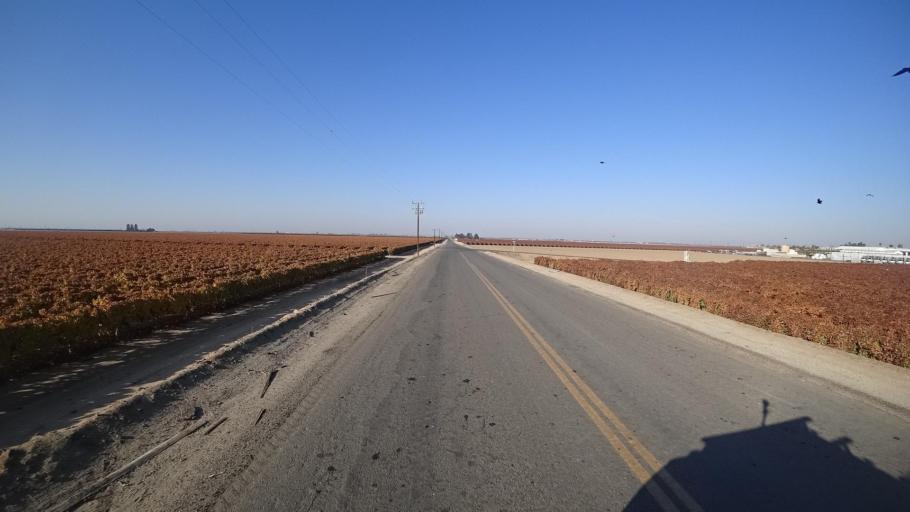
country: US
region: California
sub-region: Kern County
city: Delano
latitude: 35.7687
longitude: -119.1778
